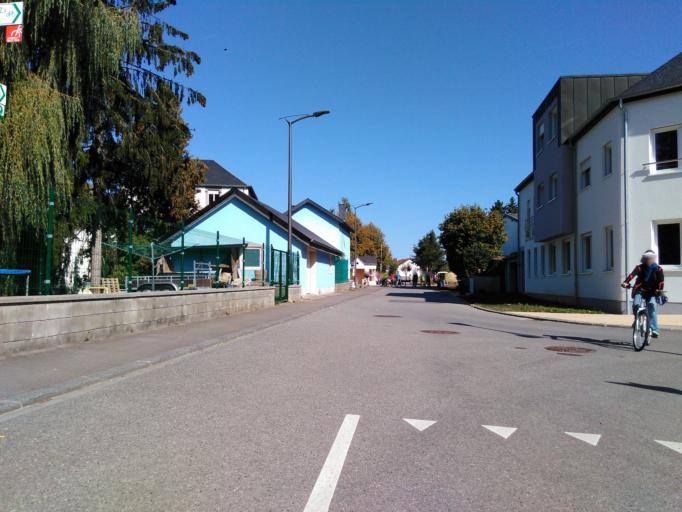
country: LU
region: Diekirch
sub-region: Canton de Redange
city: Beckerich
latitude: 49.7409
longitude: 5.9225
